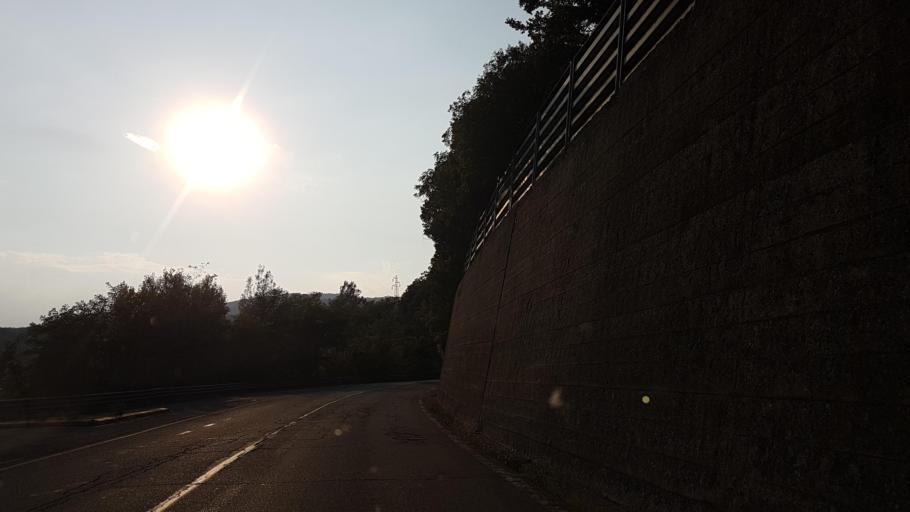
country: IT
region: Emilia-Romagna
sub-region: Provincia di Parma
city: Solignano
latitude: 44.6164
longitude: 9.9844
